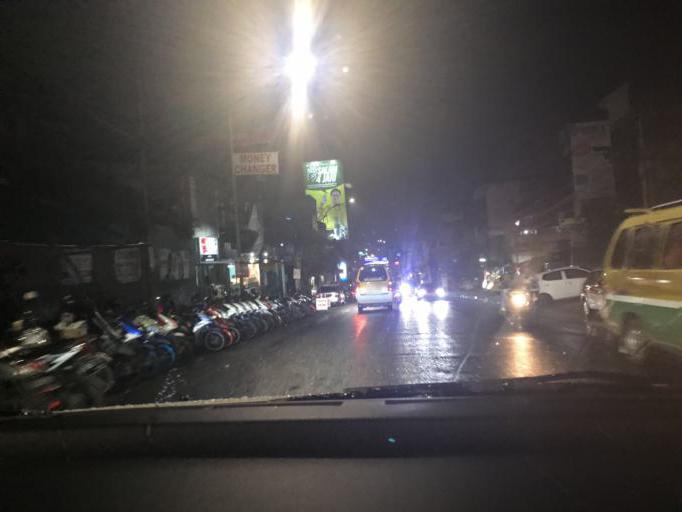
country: ID
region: West Java
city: Bandung
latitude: -6.8907
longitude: 107.5970
